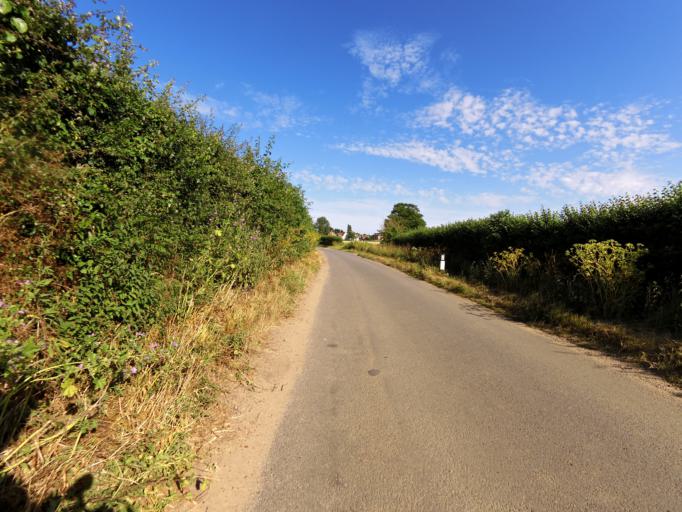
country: GB
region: England
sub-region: Suffolk
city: Leiston
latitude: 52.2694
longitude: 1.5695
